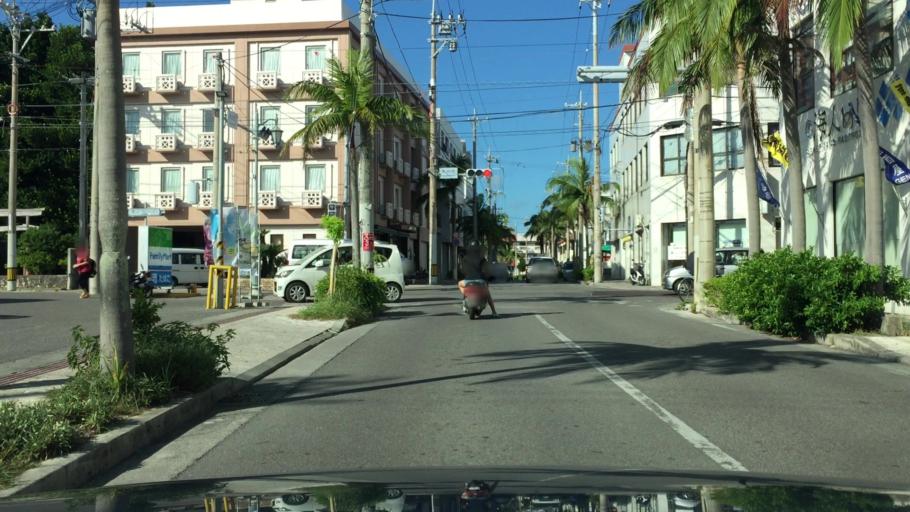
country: JP
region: Okinawa
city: Ishigaki
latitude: 24.3411
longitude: 124.1573
